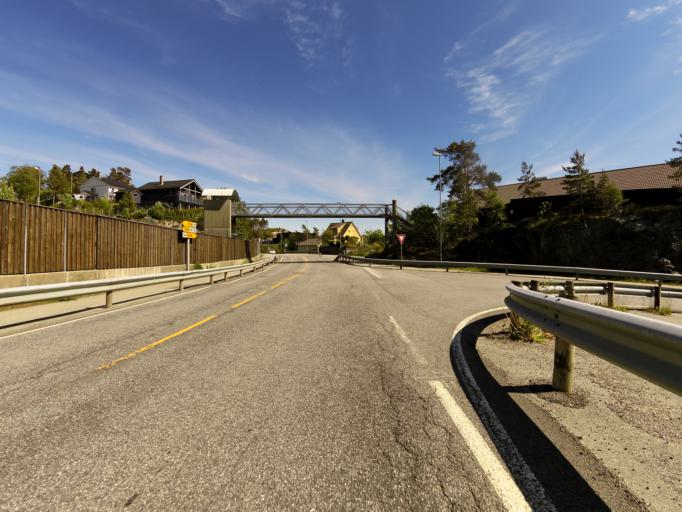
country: NO
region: Hordaland
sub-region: Stord
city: Sagvag
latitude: 59.7799
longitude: 5.3915
